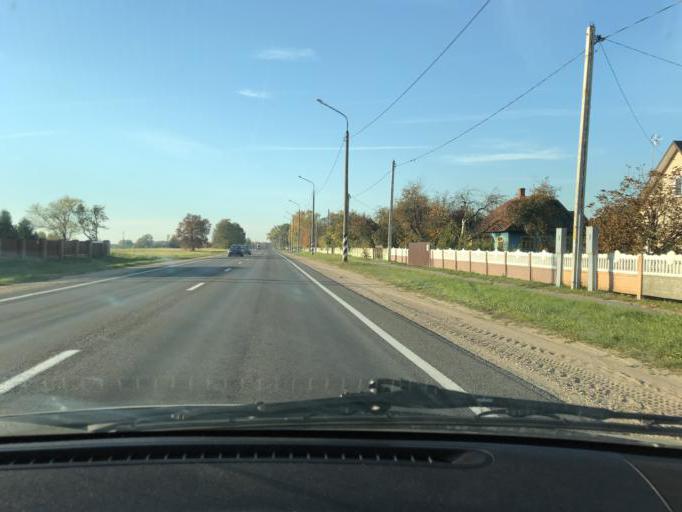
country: BY
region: Brest
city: Horad Kobryn
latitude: 52.2097
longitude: 24.5647
